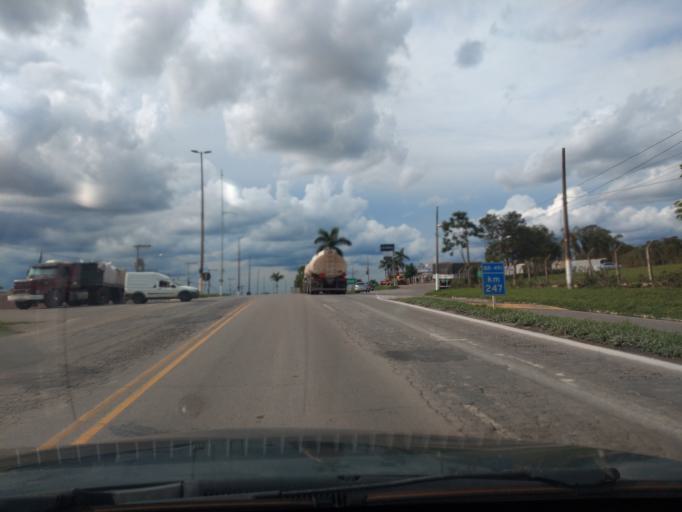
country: BR
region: Minas Gerais
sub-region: Varginha
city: Varginha
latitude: -21.5980
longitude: -45.4389
